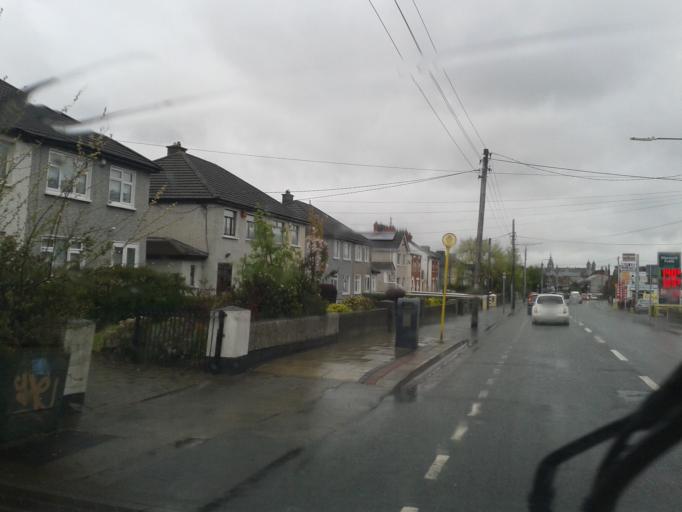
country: IE
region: Leinster
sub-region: South Dublin
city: Terenure
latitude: 53.3163
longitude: -6.2943
